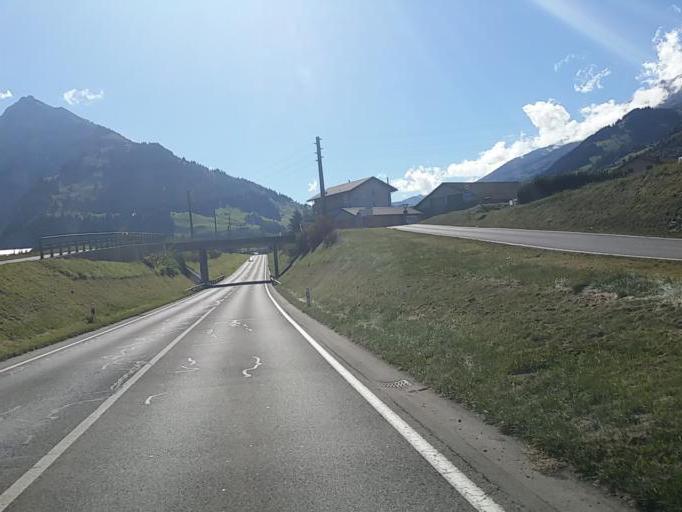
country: CH
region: Bern
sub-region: Frutigen-Niedersimmental District
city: Frutigen
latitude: 46.5925
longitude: 7.6567
